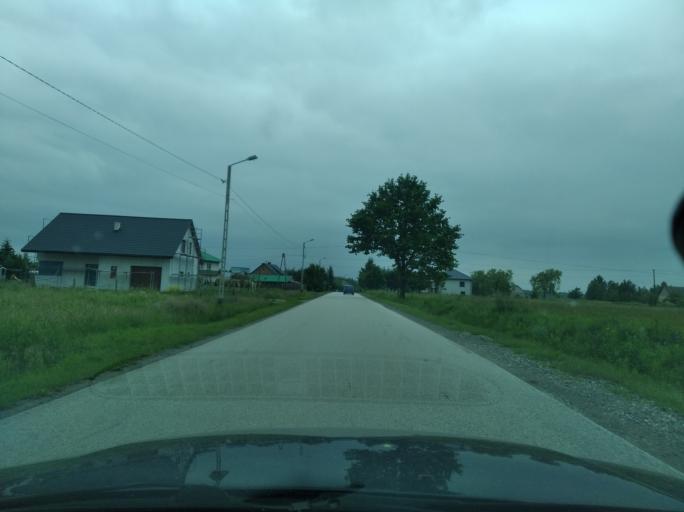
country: PL
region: Subcarpathian Voivodeship
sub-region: Powiat ropczycko-sedziszowski
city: Sedziszow Malopolski
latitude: 50.1157
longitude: 21.6745
